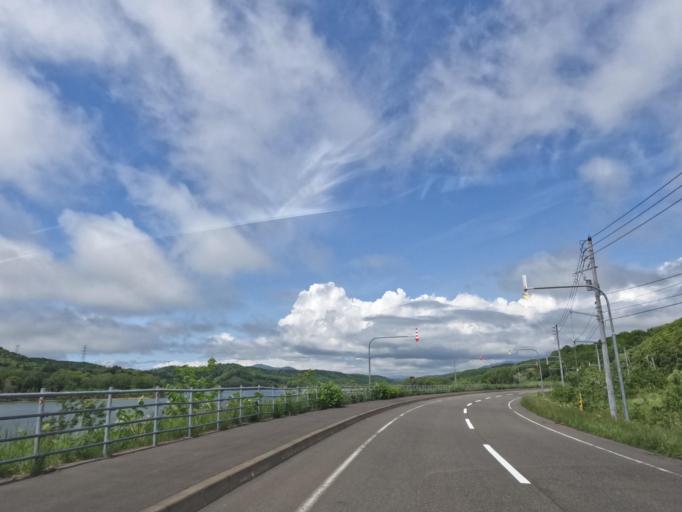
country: JP
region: Hokkaido
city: Tobetsu
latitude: 43.3608
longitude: 141.5686
